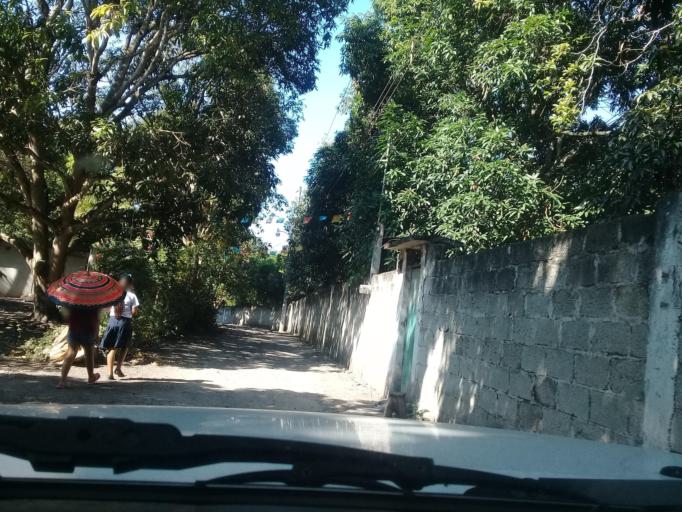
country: MX
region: Veracruz
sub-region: Emiliano Zapata
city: Plan del Rio
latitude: 19.4150
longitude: -96.6163
